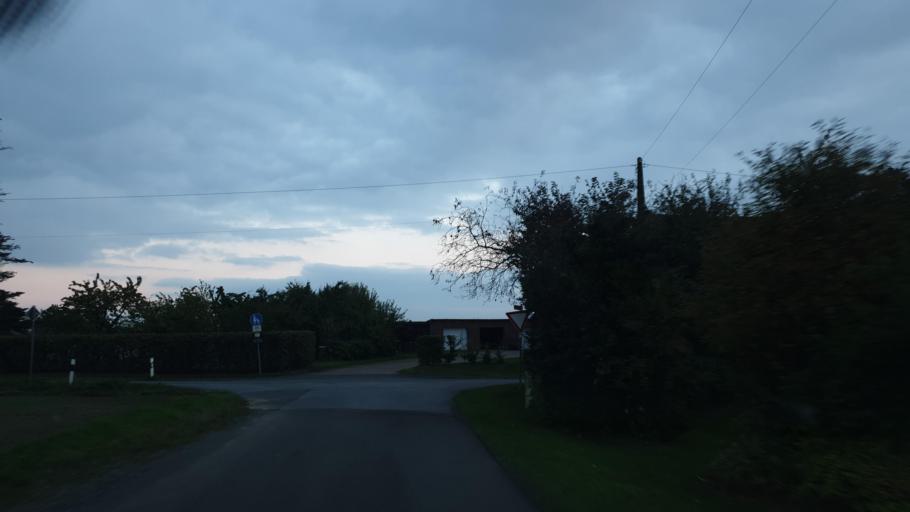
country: DE
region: North Rhine-Westphalia
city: Loehne
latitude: 52.2501
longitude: 8.7343
